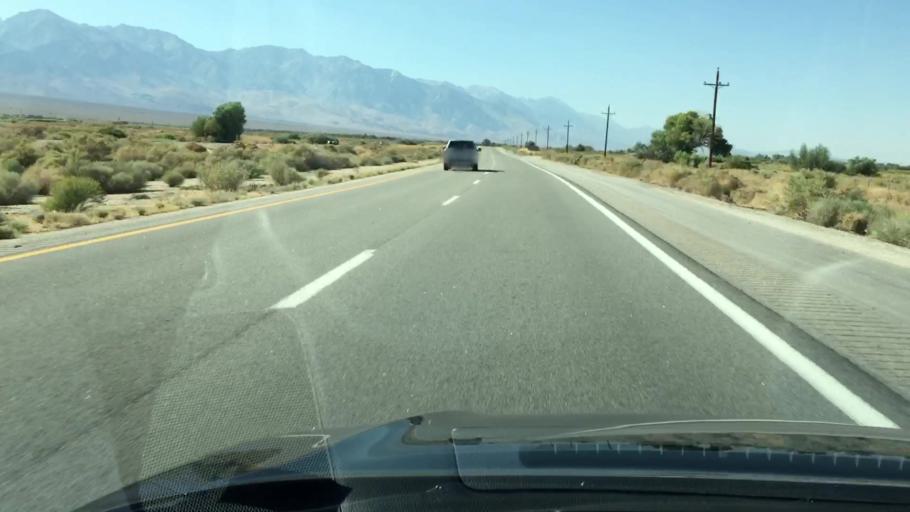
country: US
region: California
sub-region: Inyo County
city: Lone Pine
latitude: 36.6913
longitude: -118.1129
